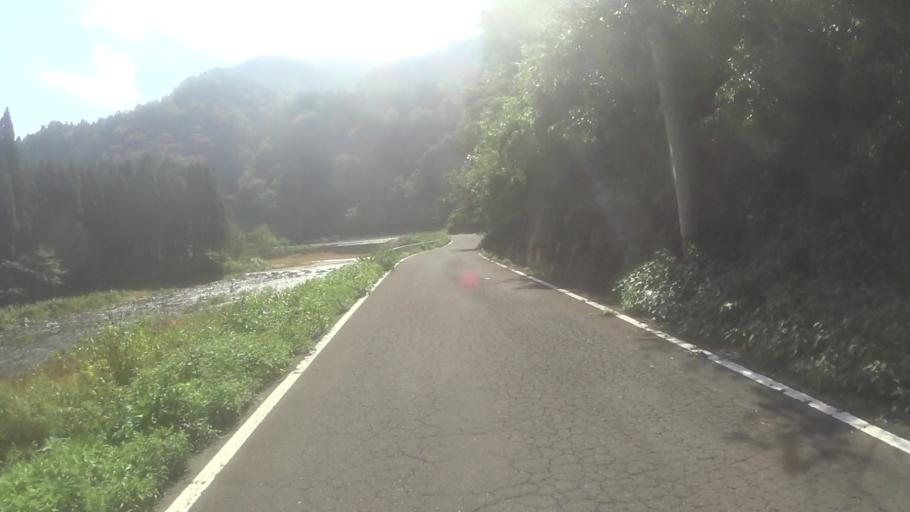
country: JP
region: Kyoto
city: Miyazu
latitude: 35.7331
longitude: 135.1577
